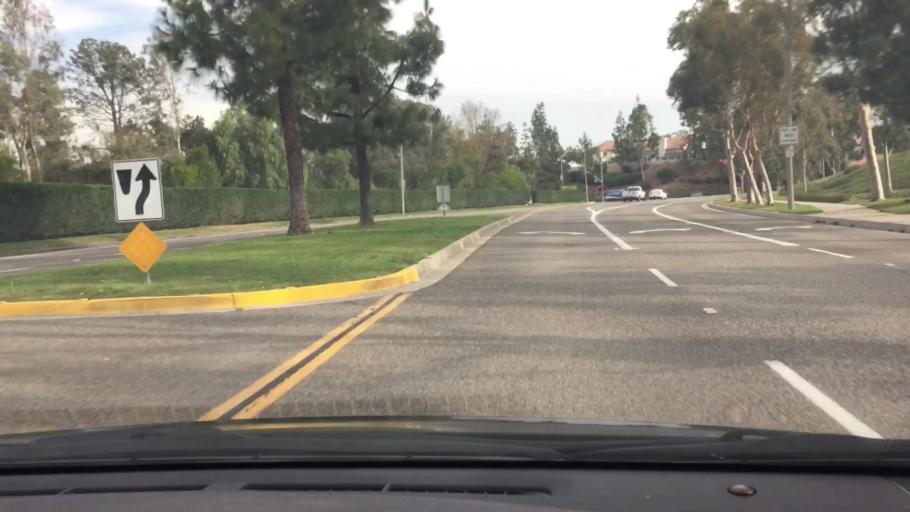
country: US
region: California
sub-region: Orange County
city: North Tustin
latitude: 33.7984
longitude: -117.7688
